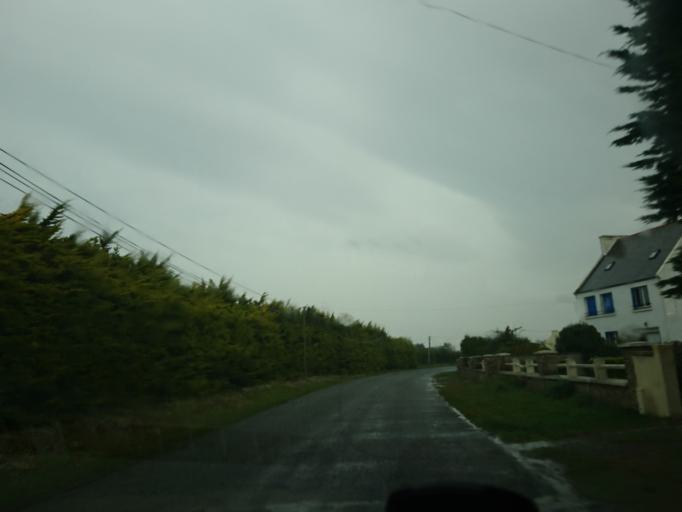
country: FR
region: Brittany
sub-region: Departement du Finistere
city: Guisseny
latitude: 48.6351
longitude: -4.4479
